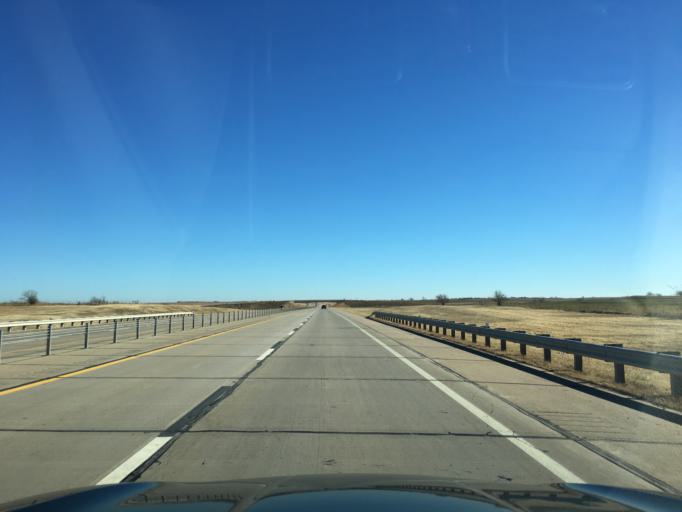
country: US
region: Oklahoma
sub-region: Noble County
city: Perry
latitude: 36.3983
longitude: -97.2361
